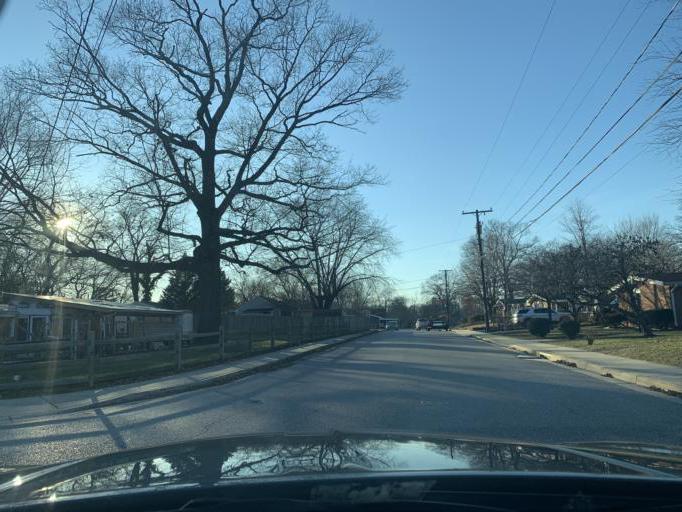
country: US
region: Maryland
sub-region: Anne Arundel County
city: Glen Burnie
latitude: 39.1465
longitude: -76.6266
